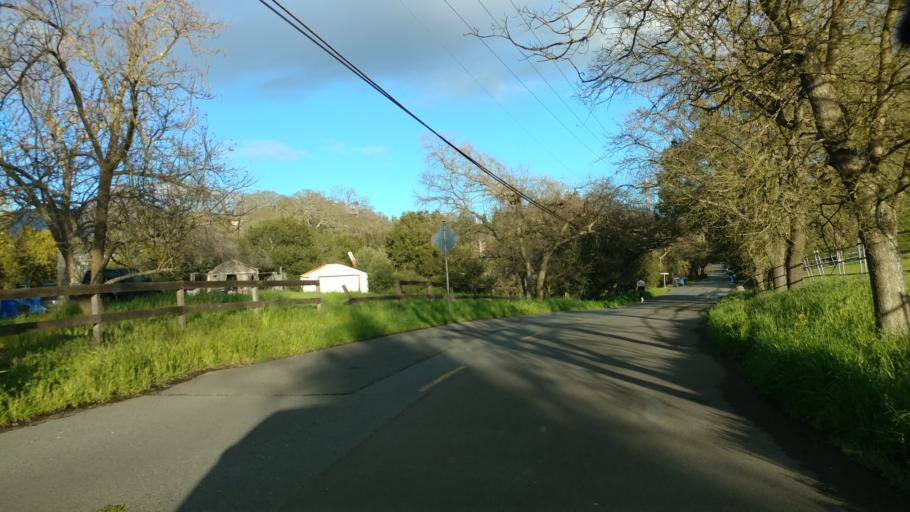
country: US
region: California
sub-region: Contra Costa County
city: Danville
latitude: 37.8436
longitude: -122.0040
